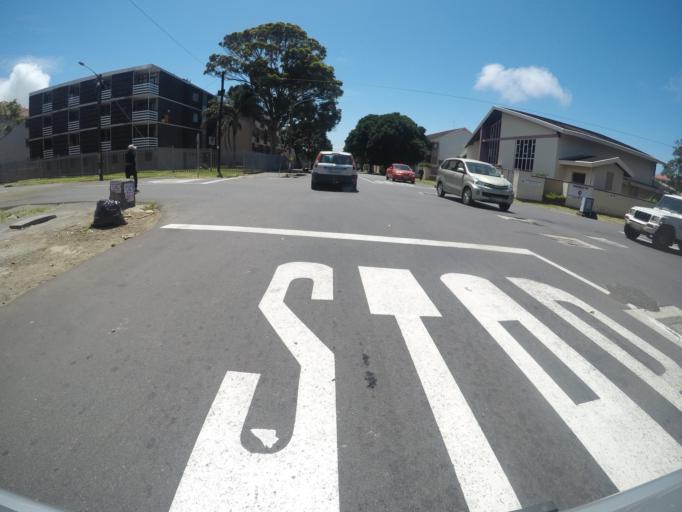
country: ZA
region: Eastern Cape
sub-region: Buffalo City Metropolitan Municipality
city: East London
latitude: -33.0046
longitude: 27.9035
